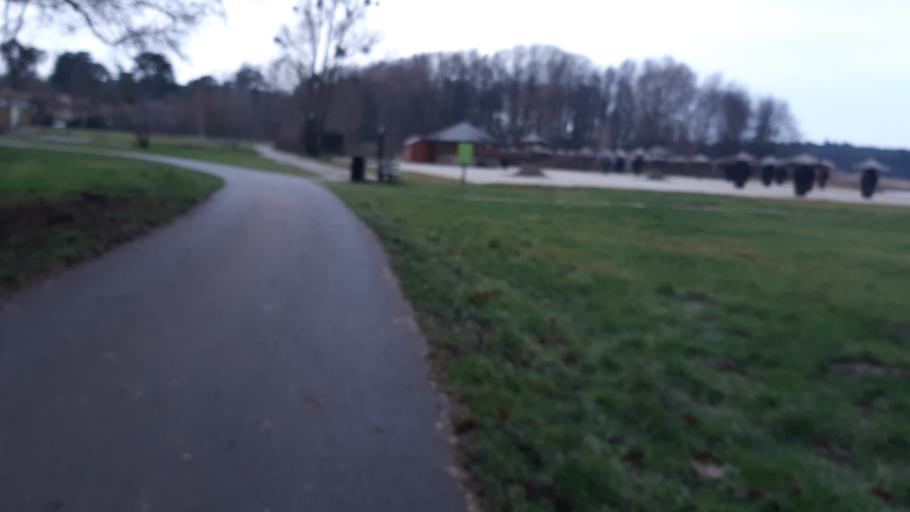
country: DE
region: Brandenburg
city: Templin
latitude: 53.1106
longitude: 13.5368
